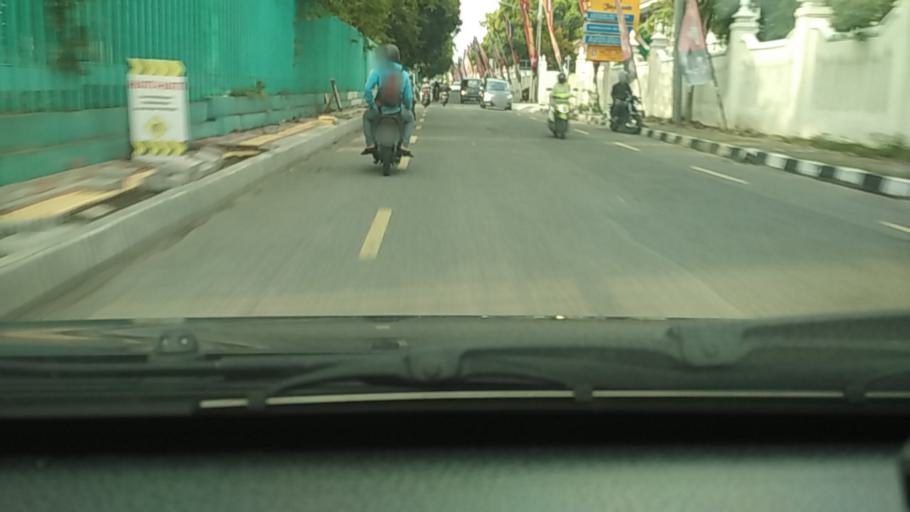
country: ID
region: Daerah Istimewa Yogyakarta
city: Yogyakarta
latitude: -7.7974
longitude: 110.3851
